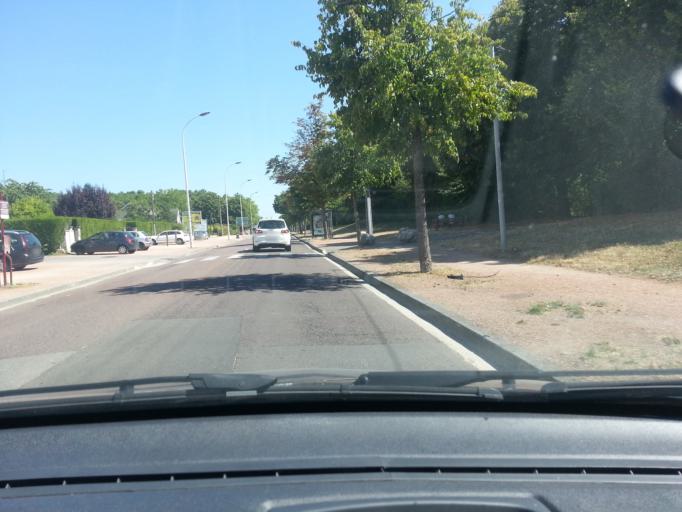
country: FR
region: Bourgogne
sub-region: Departement de la Cote-d'Or
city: Longvic
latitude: 47.3049
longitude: 5.0618
